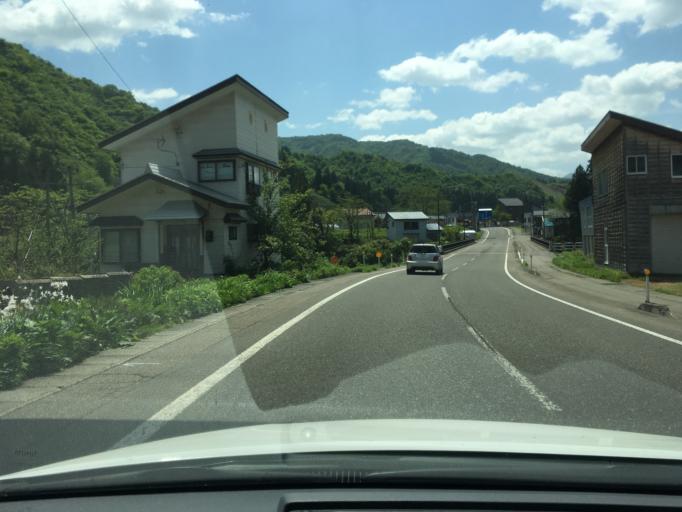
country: JP
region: Niigata
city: Tochio-honcho
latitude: 37.3496
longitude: 139.0488
